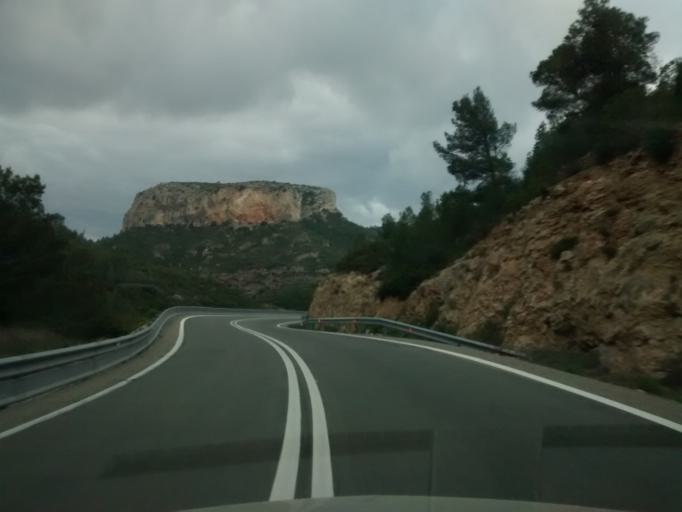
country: ES
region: Catalonia
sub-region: Provincia de Tarragona
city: Gandesa
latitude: 41.0396
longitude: 0.4853
